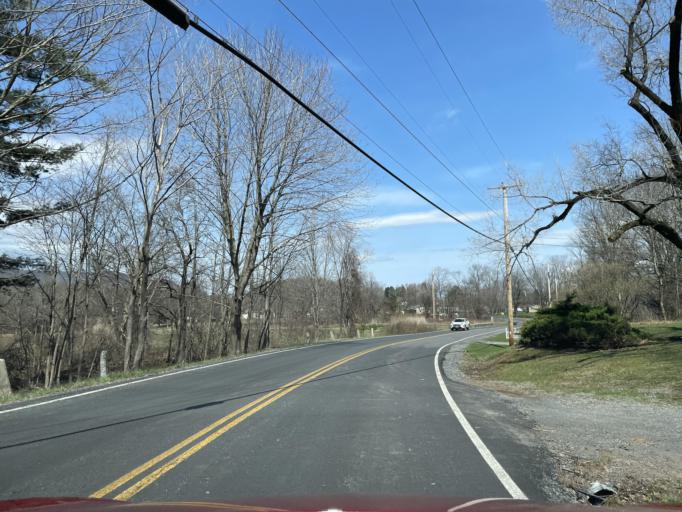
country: US
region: New York
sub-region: Ulster County
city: Manorville
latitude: 42.1262
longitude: -74.0214
